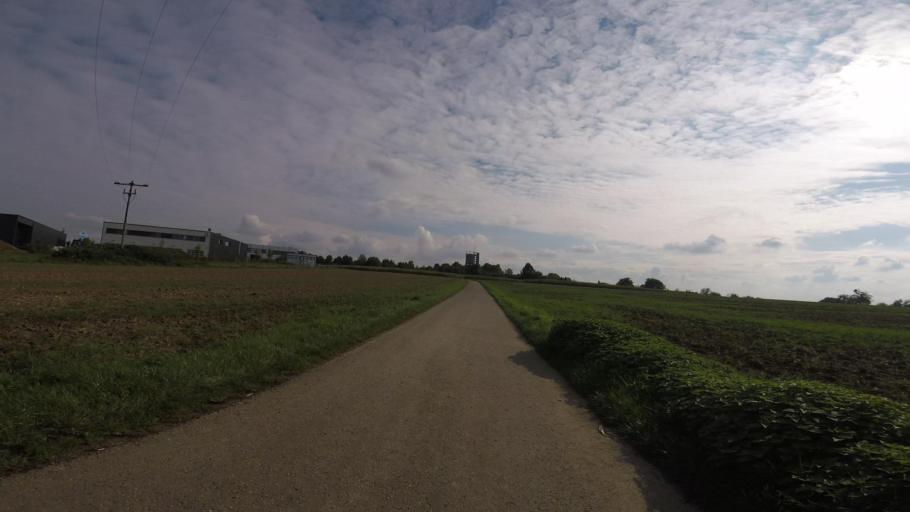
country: DE
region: Baden-Wuerttemberg
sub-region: Regierungsbezirk Stuttgart
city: Backnang
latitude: 48.9601
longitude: 9.4202
